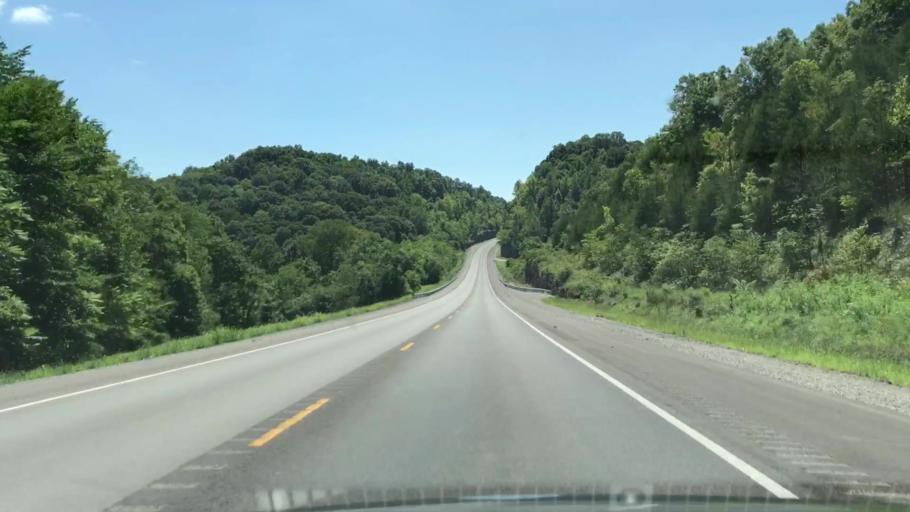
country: US
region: Kentucky
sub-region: Cumberland County
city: Burkesville
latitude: 36.6768
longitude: -85.3708
